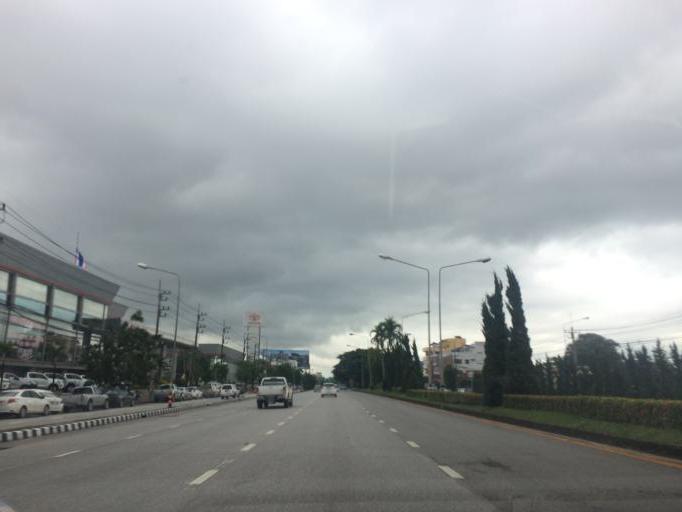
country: TH
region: Chiang Rai
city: Chiang Rai
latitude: 19.8920
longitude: 99.8370
